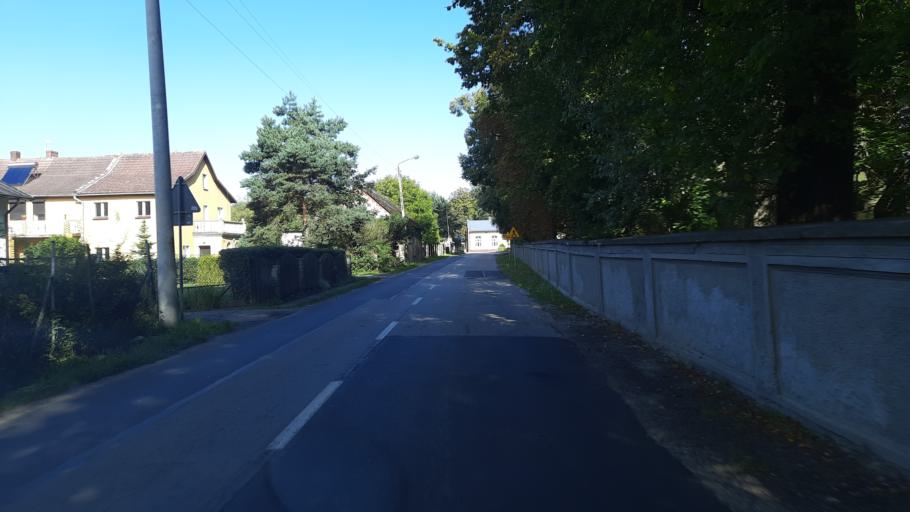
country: PL
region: Lower Silesian Voivodeship
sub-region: Powiat wroclawski
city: Dlugoleka
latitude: 51.1932
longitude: 17.1839
